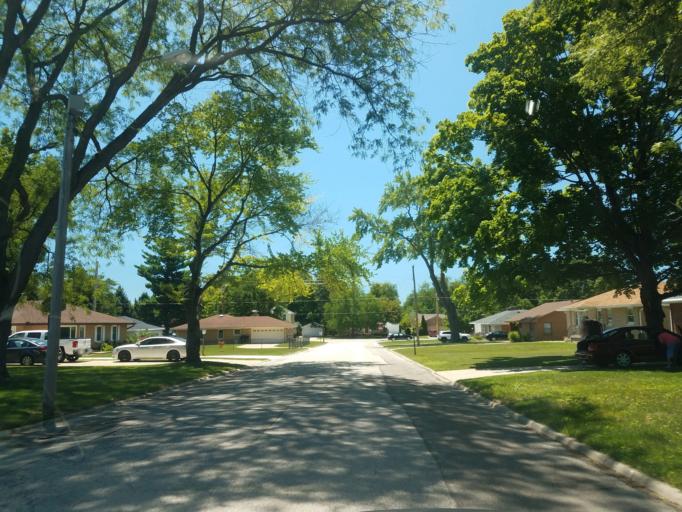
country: US
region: Illinois
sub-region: McLean County
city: Normal
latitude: 40.5109
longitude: -89.0032
